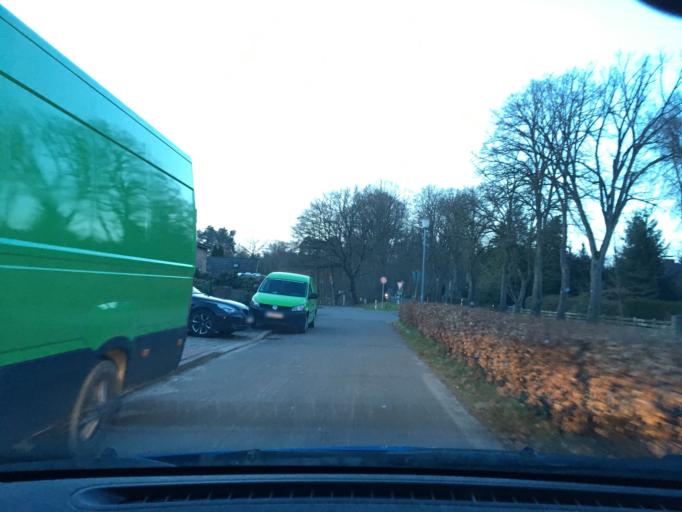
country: DE
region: Lower Saxony
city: Egestorf
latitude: 53.1798
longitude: 10.0639
